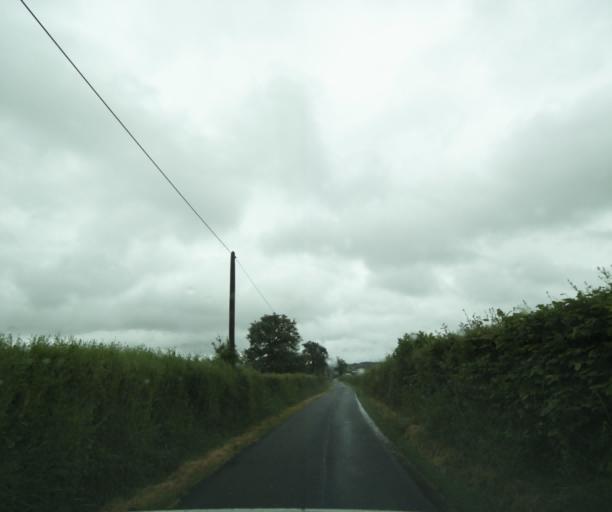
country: FR
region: Bourgogne
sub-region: Departement de Saone-et-Loire
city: Charolles
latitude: 46.4815
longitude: 4.4272
